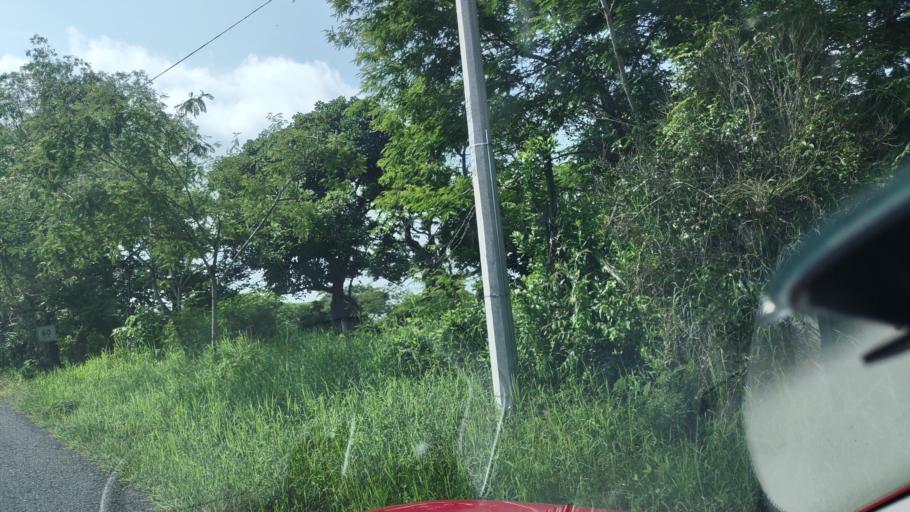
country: MX
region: Veracruz
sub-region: Emiliano Zapata
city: Dos Rios
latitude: 19.4505
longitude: -96.8258
